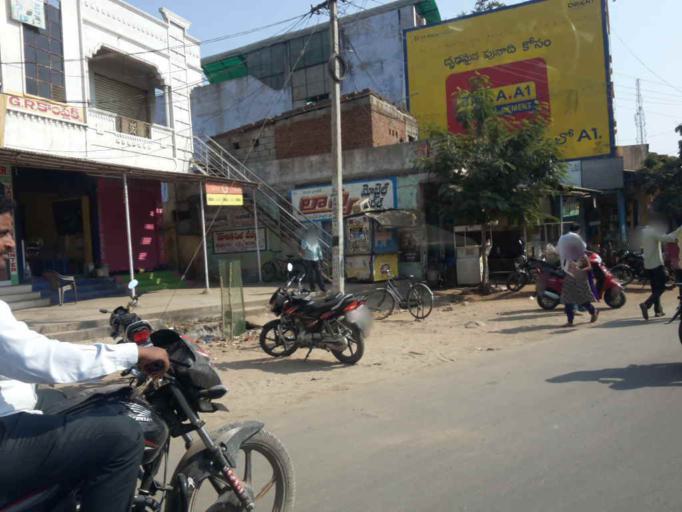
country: IN
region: Telangana
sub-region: Karimnagar
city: Koratla
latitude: 18.8487
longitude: 78.6209
